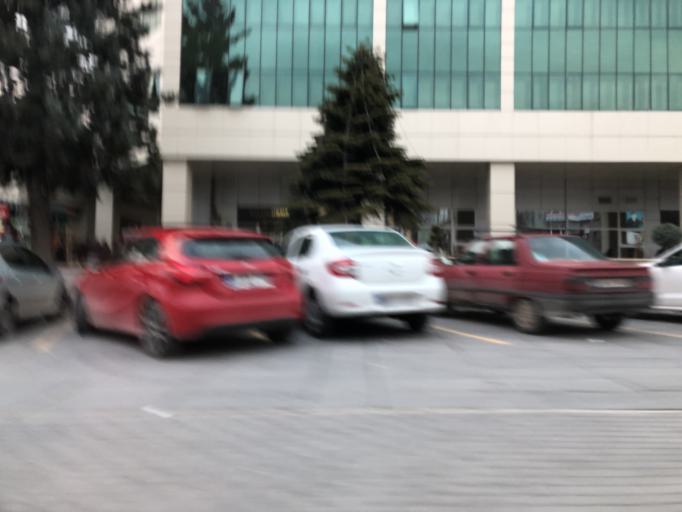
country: TR
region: Ankara
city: Ankara
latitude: 39.9625
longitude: 32.8104
